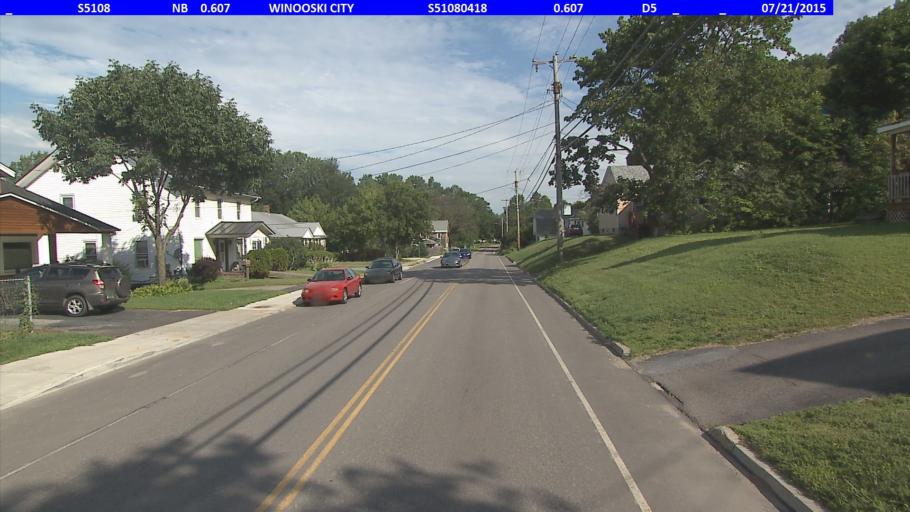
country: US
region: Vermont
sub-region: Chittenden County
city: Winooski
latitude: 44.4985
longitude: -73.1959
